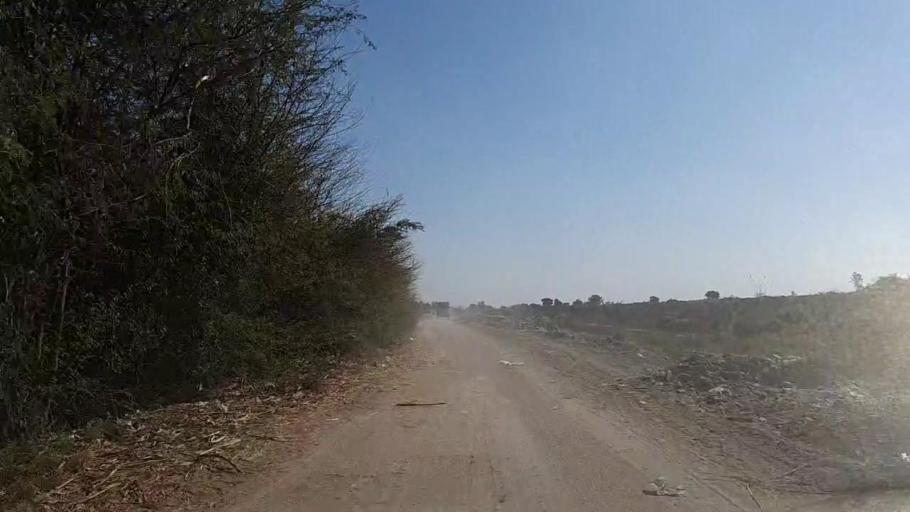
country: PK
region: Sindh
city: Nawabshah
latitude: 26.2382
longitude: 68.4246
